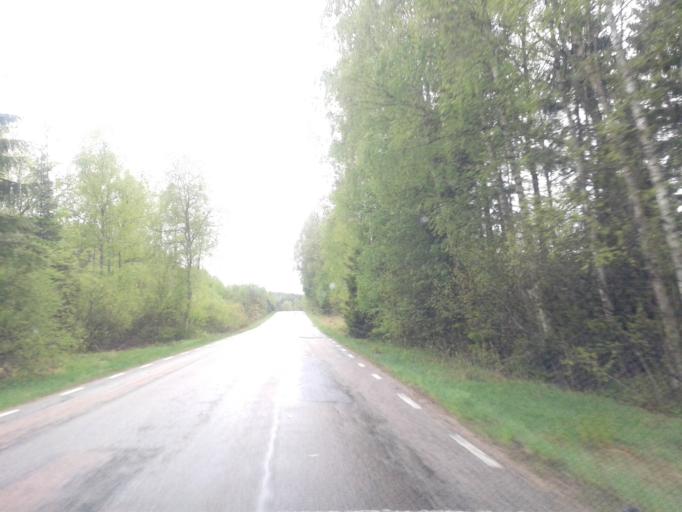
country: SE
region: Vaestra Goetaland
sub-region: Lilla Edets Kommun
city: Lilla Edet
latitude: 58.0880
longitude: 12.0668
